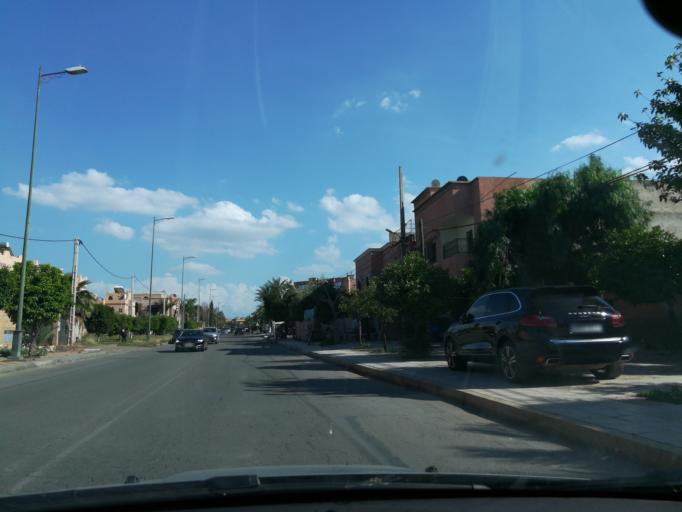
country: MA
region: Marrakech-Tensift-Al Haouz
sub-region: Marrakech
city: Marrakesh
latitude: 31.6560
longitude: -8.0531
